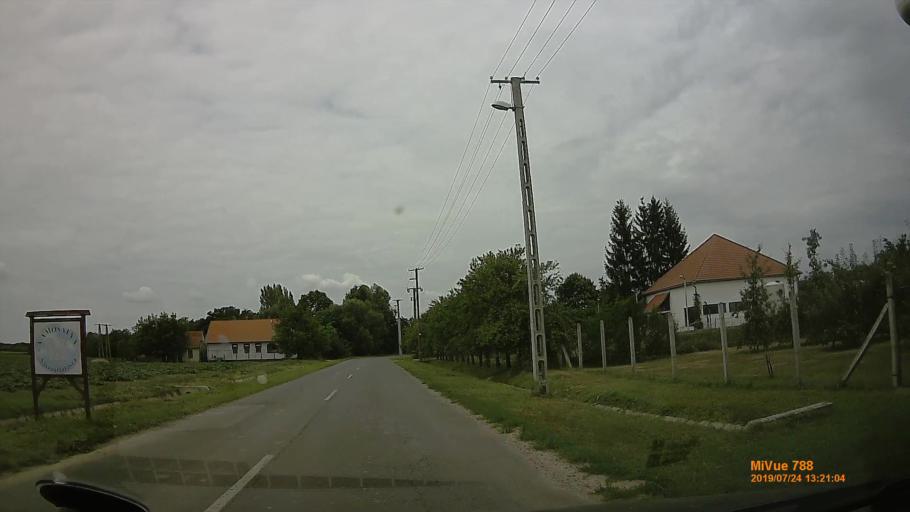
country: HU
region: Szabolcs-Szatmar-Bereg
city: Vasarosnameny
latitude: 48.2054
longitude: 22.4138
